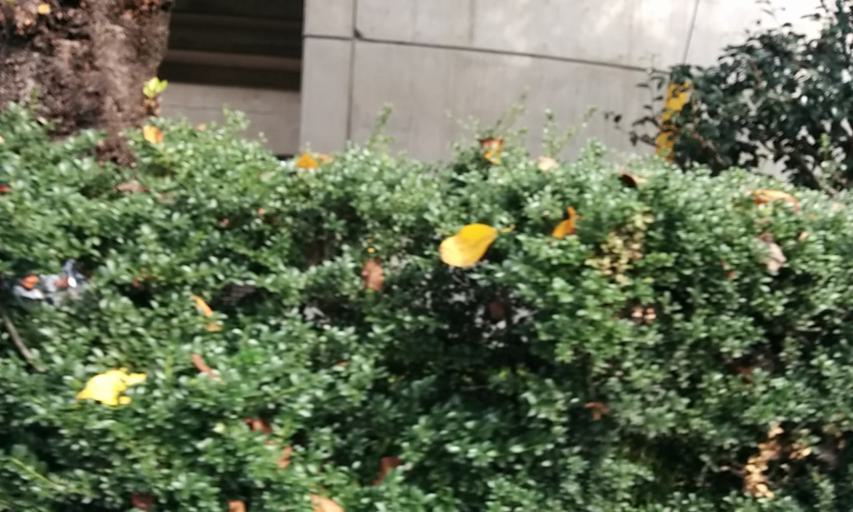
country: JP
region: Tokyo
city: Kokubunji
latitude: 35.6759
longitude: 139.4742
